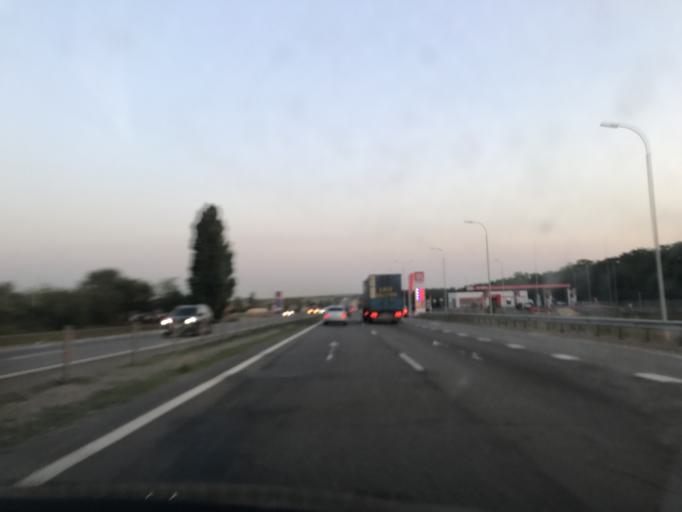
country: RU
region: Rostov
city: Grushevskaya
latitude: 47.5390
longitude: 39.9686
